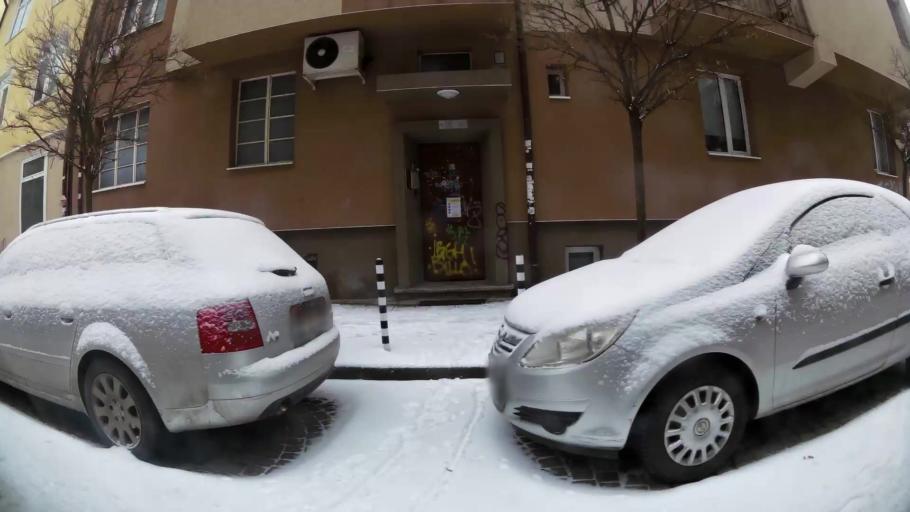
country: BG
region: Sofia-Capital
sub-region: Stolichna Obshtina
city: Sofia
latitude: 42.6902
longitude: 23.3157
